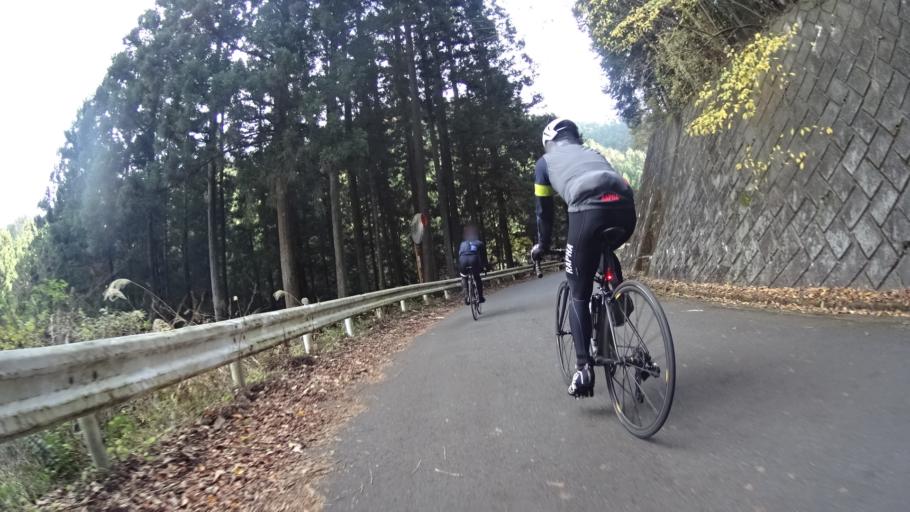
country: JP
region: Saitama
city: Chichibu
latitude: 35.9176
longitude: 139.1777
